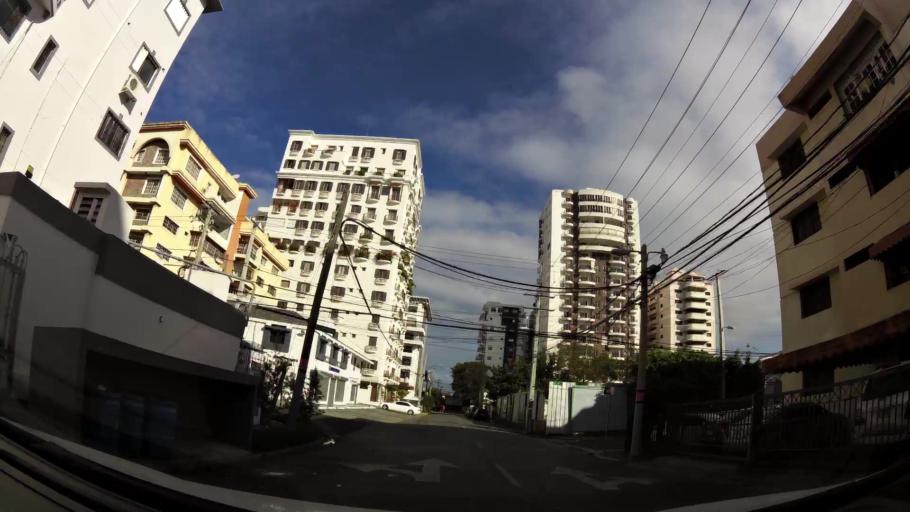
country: DO
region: Nacional
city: La Julia
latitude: 18.4807
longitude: -69.9413
